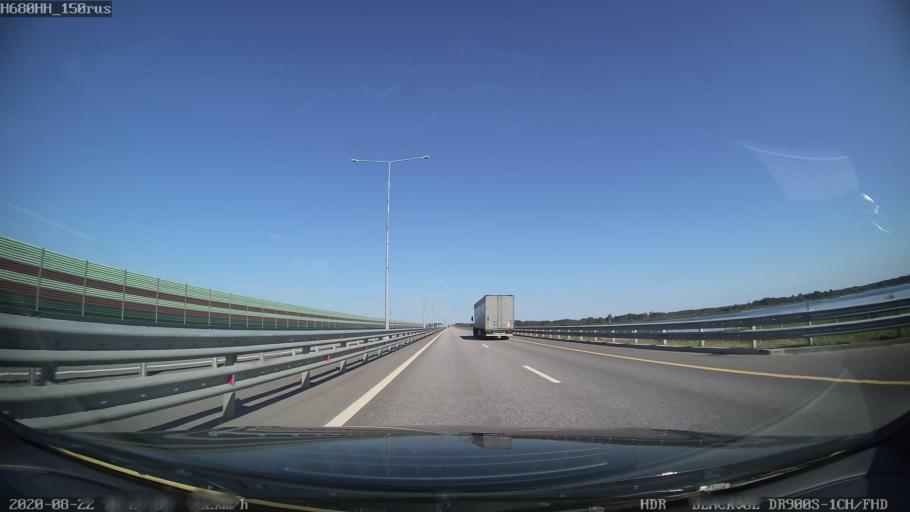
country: RU
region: Tverskaya
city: Novozavidovskiy
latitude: 56.5939
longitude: 36.4630
